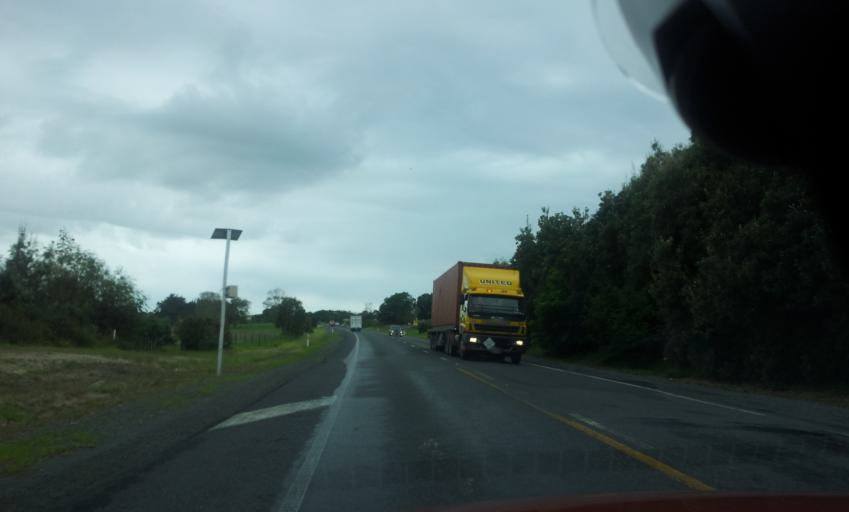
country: NZ
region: Northland
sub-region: Whangarei
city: Ruakaka
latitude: -35.9451
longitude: 174.4553
